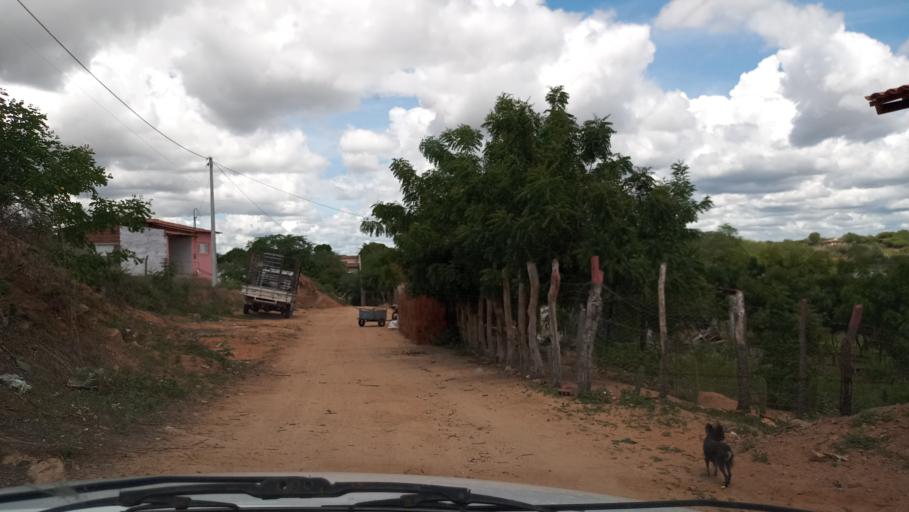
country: BR
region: Rio Grande do Norte
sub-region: Sao Paulo Do Potengi
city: Sao Paulo do Potengi
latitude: -5.8949
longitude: -35.7696
